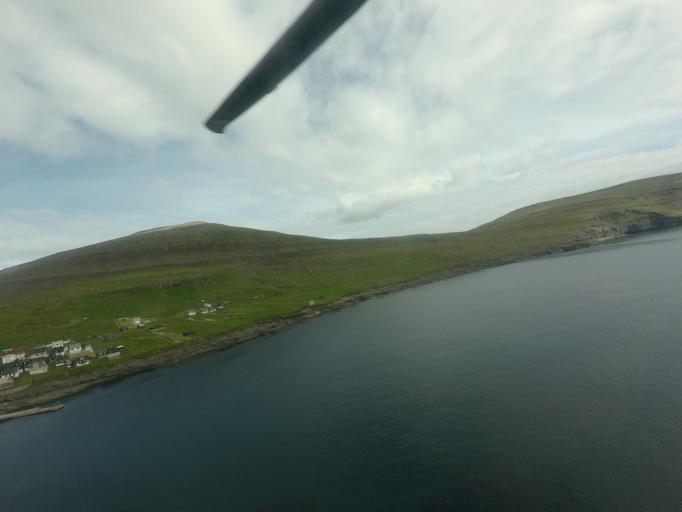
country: FO
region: Nordoyar
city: Klaksvik
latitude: 62.2757
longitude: -6.3368
